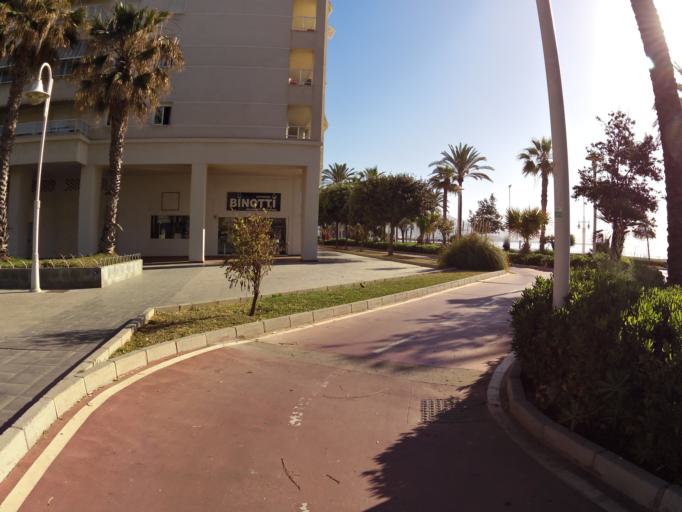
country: ES
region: Andalusia
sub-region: Provincia de Malaga
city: Malaga
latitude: 36.6903
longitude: -4.4421
